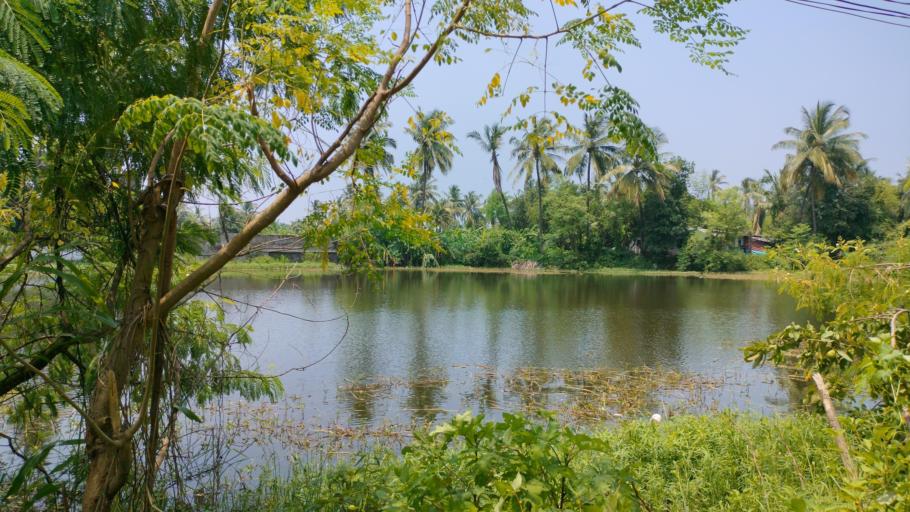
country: IN
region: Maharashtra
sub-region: Thane
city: Virar
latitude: 19.3874
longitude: 72.7734
